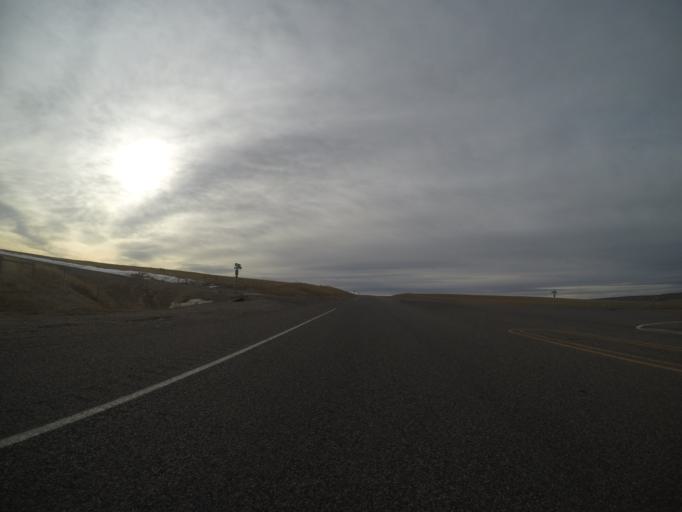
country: US
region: Montana
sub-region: Yellowstone County
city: Laurel
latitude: 45.5593
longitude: -108.8578
